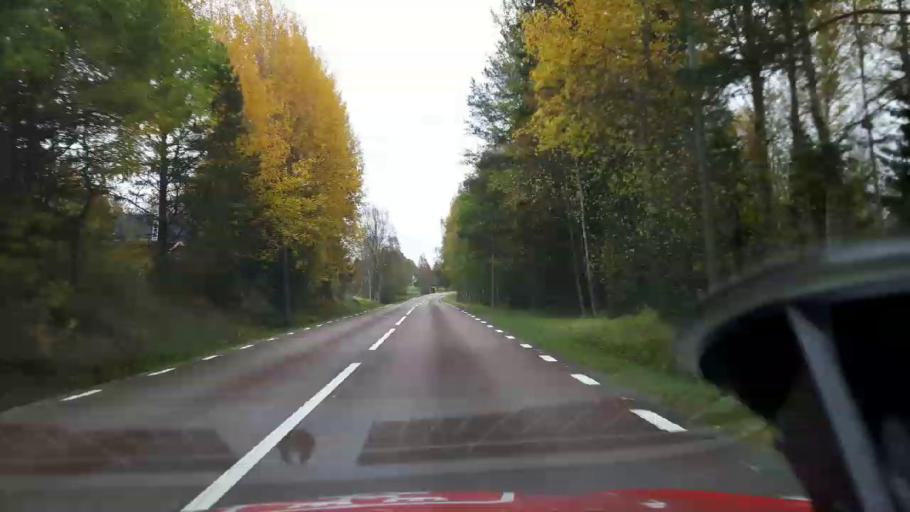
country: SE
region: Jaemtland
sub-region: Harjedalens Kommun
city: Sveg
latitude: 62.3100
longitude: 14.7600
